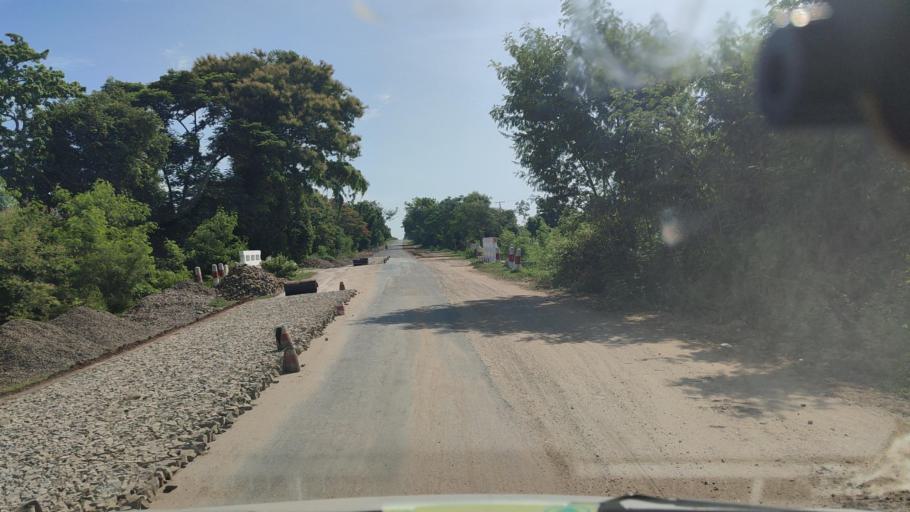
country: MM
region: Magway
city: Minbu
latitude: 20.1500
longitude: 94.7945
